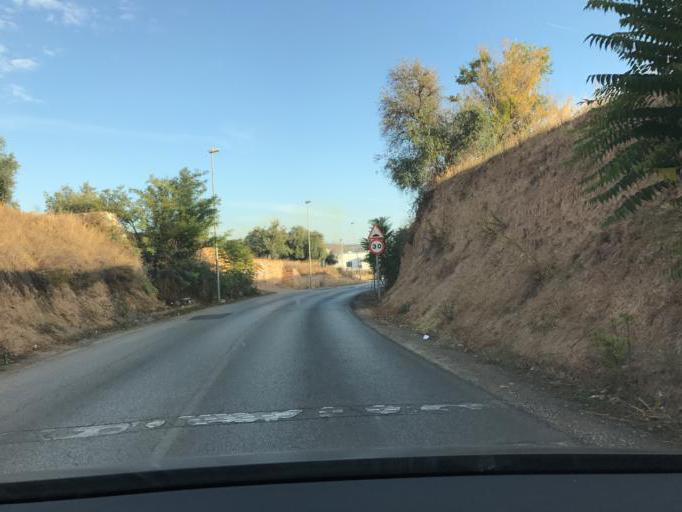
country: ES
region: Andalusia
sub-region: Provincia de Granada
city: Pulianas
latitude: 37.2258
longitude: -3.6099
